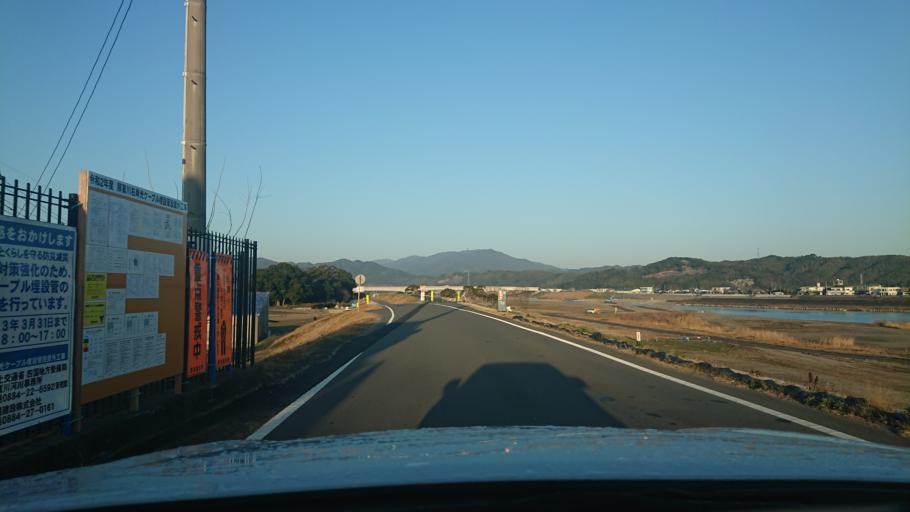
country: JP
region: Tokushima
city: Anan
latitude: 33.9381
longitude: 134.6210
